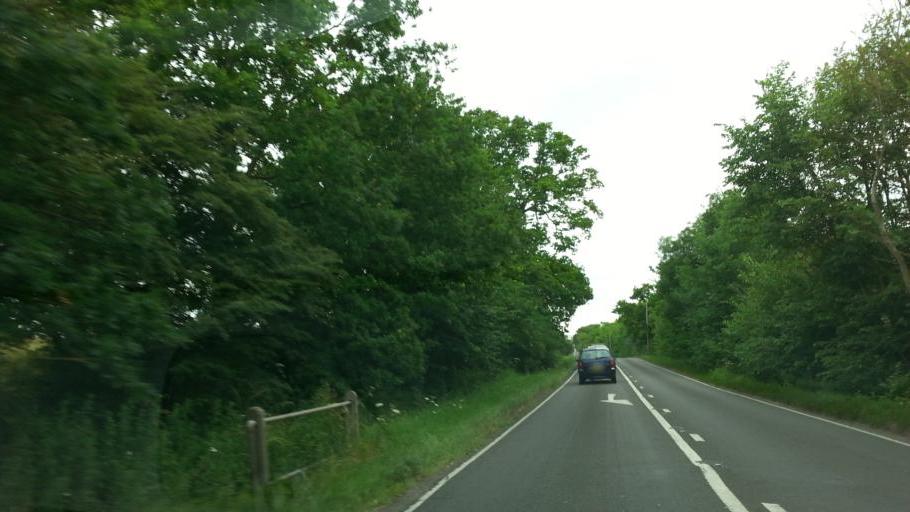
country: GB
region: England
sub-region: Cambridgeshire
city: Papworth Everard
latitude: 52.2370
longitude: -0.1091
